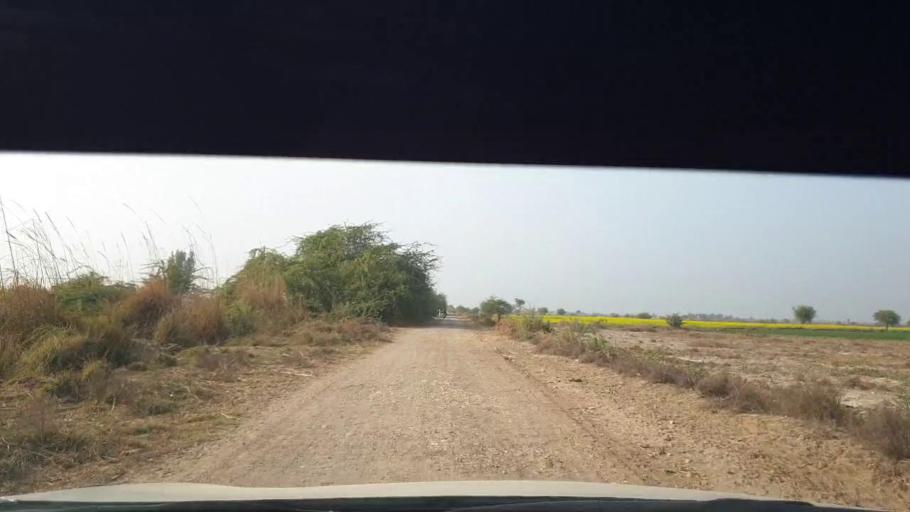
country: PK
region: Sindh
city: Berani
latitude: 25.7488
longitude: 68.9442
